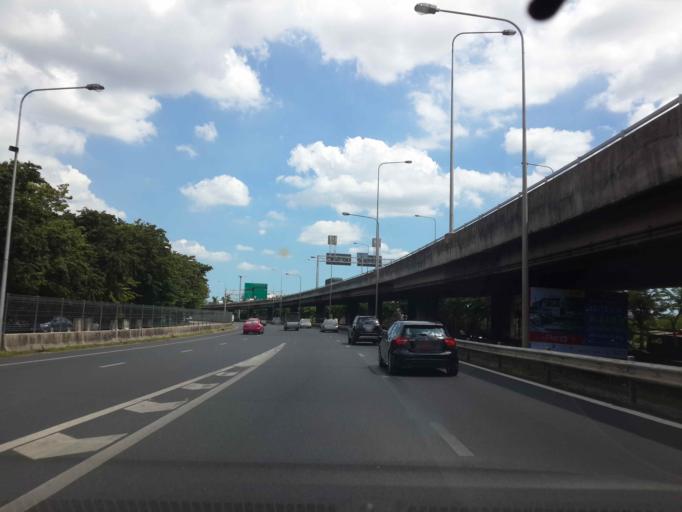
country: TH
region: Bangkok
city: Chom Thong
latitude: 13.6784
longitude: 100.4778
